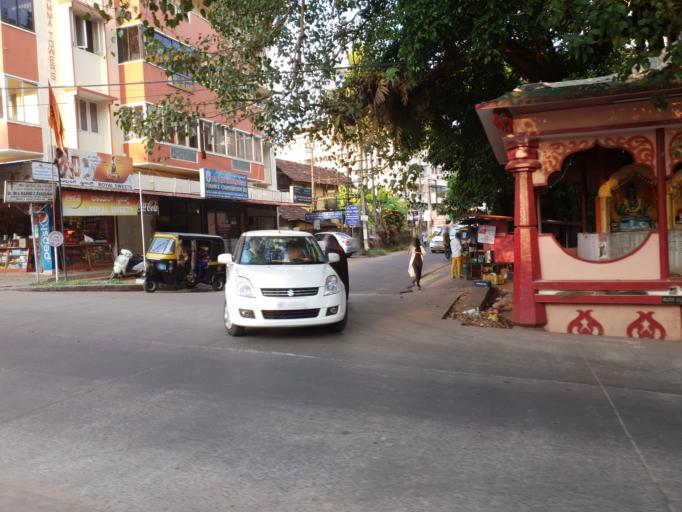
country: IN
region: Karnataka
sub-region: Dakshina Kannada
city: Ullal
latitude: 12.8559
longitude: 74.8397
